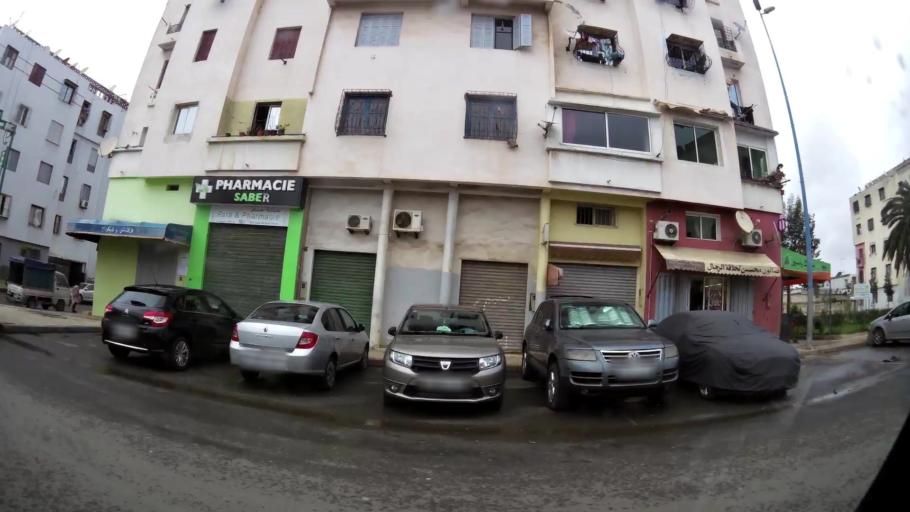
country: MA
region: Grand Casablanca
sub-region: Casablanca
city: Casablanca
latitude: 33.5336
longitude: -7.6484
